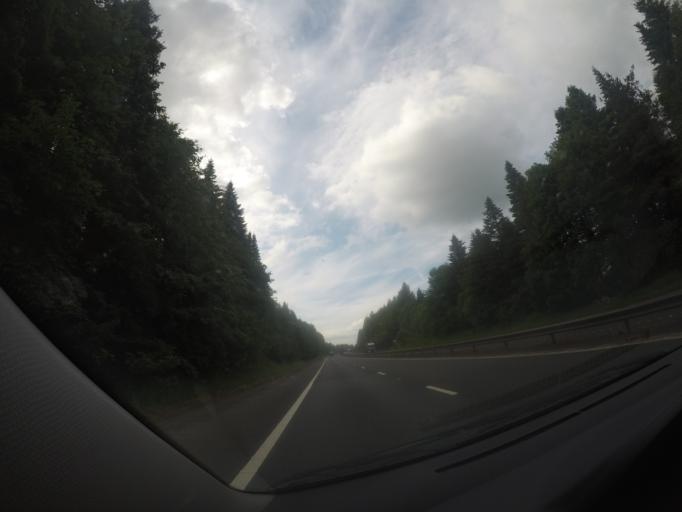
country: GB
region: Scotland
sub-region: South Lanarkshire
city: Douglas
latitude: 55.5791
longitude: -3.8186
